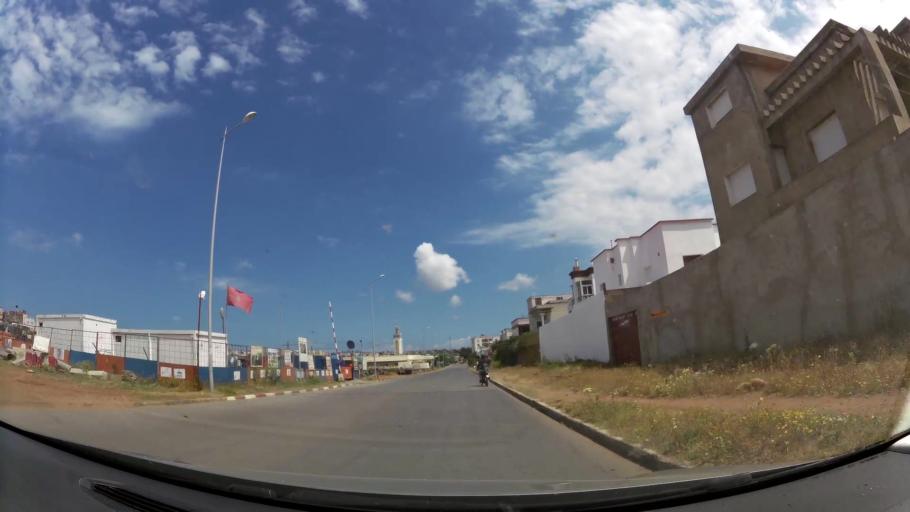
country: MA
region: Gharb-Chrarda-Beni Hssen
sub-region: Kenitra Province
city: Kenitra
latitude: 34.2449
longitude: -6.6075
